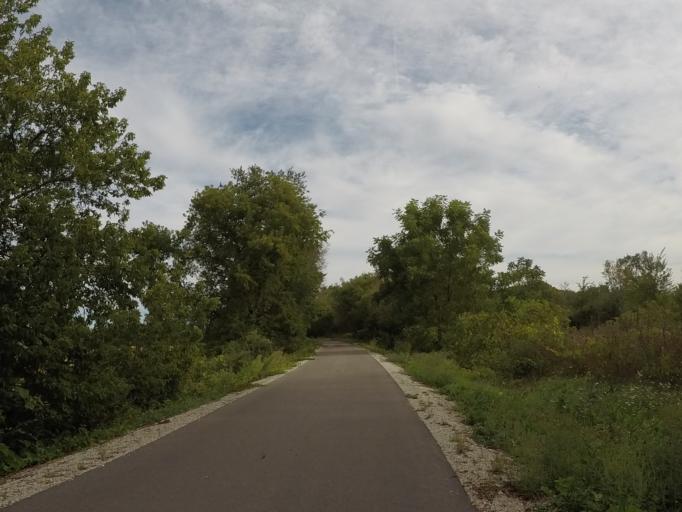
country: US
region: Wisconsin
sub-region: Sauk County
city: Prairie du Sac
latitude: 43.3442
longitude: -89.7415
